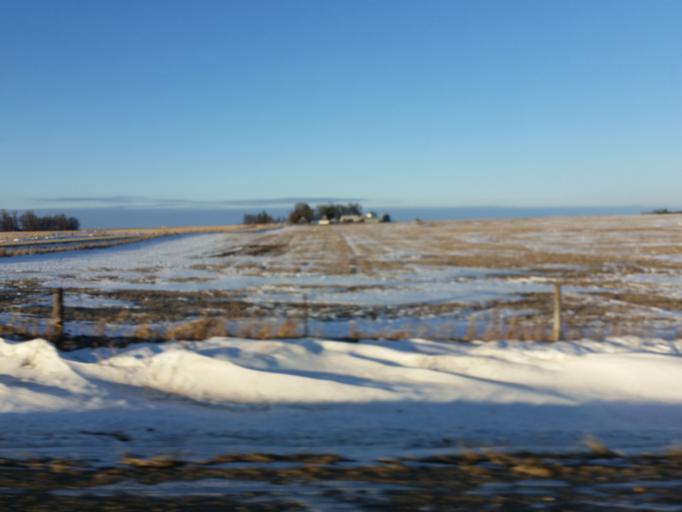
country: US
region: Iowa
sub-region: Butler County
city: Allison
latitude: 42.7450
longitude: -92.8885
